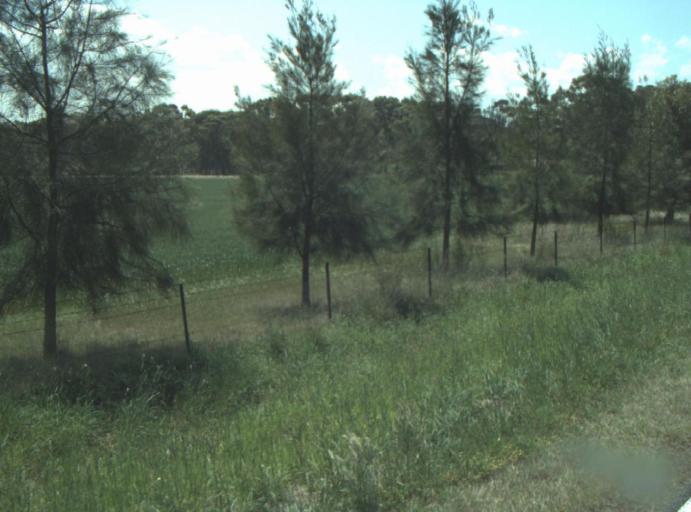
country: AU
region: Victoria
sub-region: Greater Geelong
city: Lara
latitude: -37.9667
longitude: 144.4063
